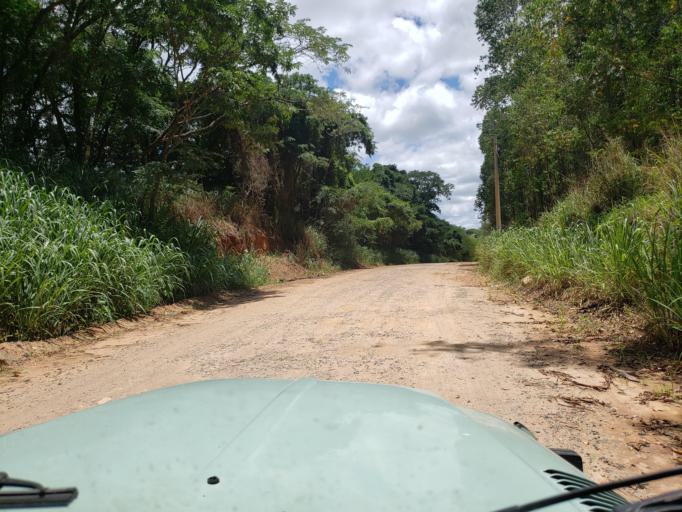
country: BR
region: Sao Paulo
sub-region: Moji-Guacu
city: Mogi-Gaucu
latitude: -22.2535
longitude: -46.8491
